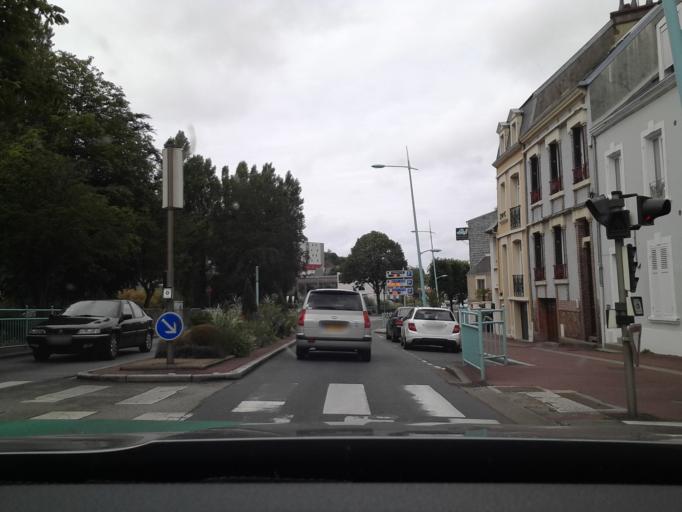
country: FR
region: Lower Normandy
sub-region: Departement de la Manche
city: Cherbourg-Octeville
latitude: 49.6279
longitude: -1.6179
